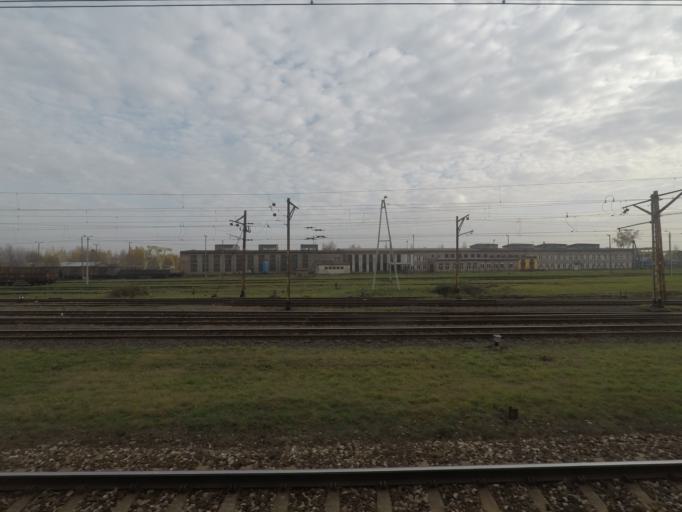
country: PL
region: Subcarpathian Voivodeship
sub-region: Powiat przemyski
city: Orly
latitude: 49.8351
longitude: 22.8394
